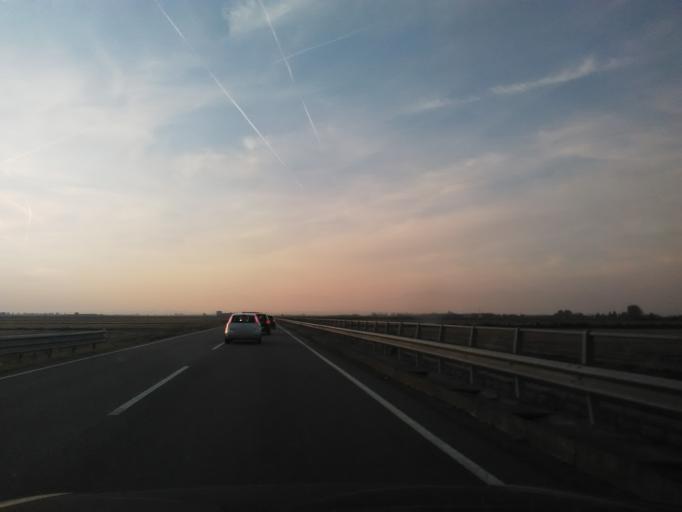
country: IT
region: Piedmont
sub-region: Provincia di Vercelli
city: Olcenengo
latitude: 45.3351
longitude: 8.3057
